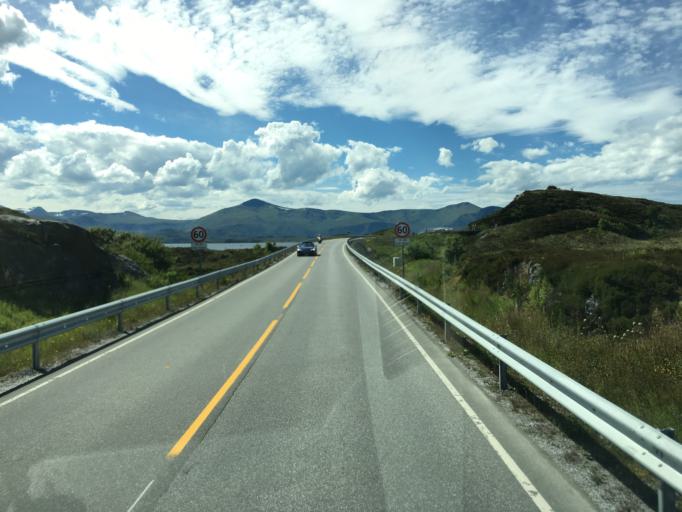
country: NO
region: More og Romsdal
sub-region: Eide
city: Eide
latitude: 63.0198
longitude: 7.3699
